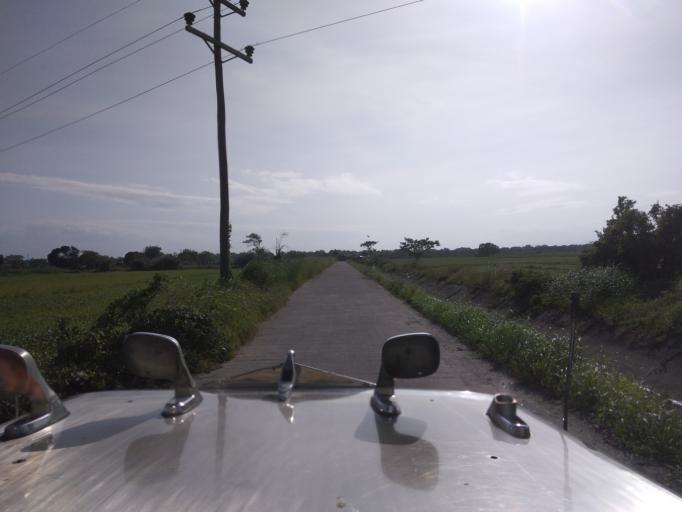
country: PH
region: Central Luzon
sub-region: Province of Pampanga
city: San Patricio
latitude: 15.1018
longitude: 120.7019
